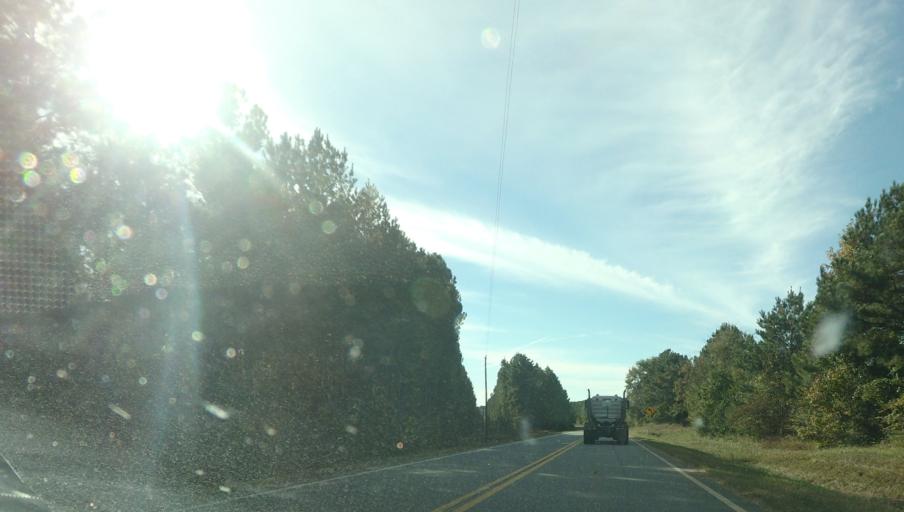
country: US
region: Georgia
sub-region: Talbot County
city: Talbotton
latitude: 32.7049
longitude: -84.4019
